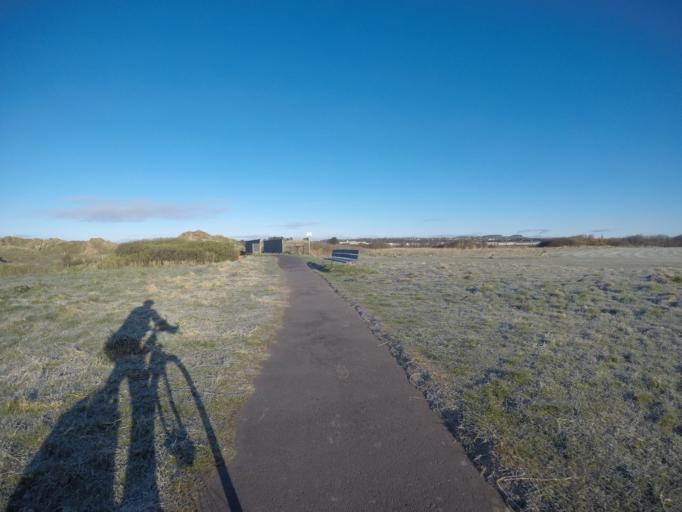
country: GB
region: Scotland
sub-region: North Ayrshire
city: Stevenston
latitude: 55.6311
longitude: -4.7559
